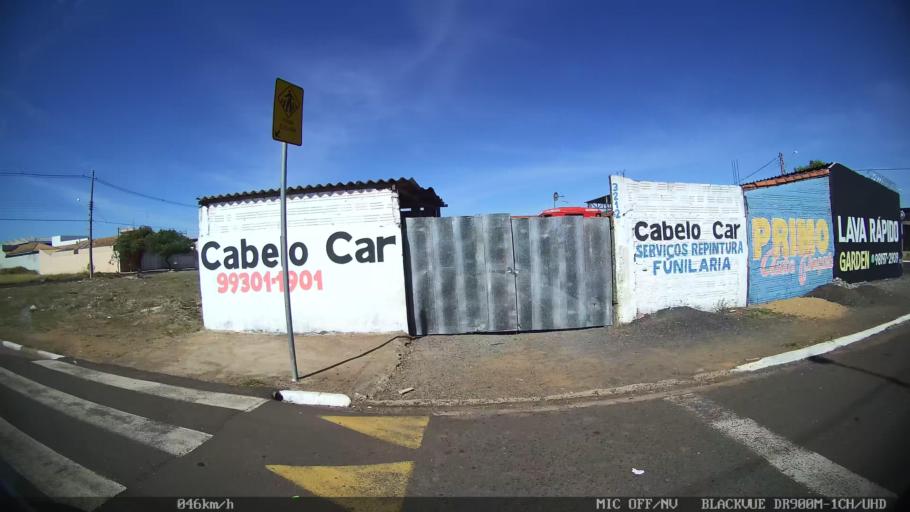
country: BR
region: Sao Paulo
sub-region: Franca
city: Franca
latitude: -20.5425
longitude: -47.3779
